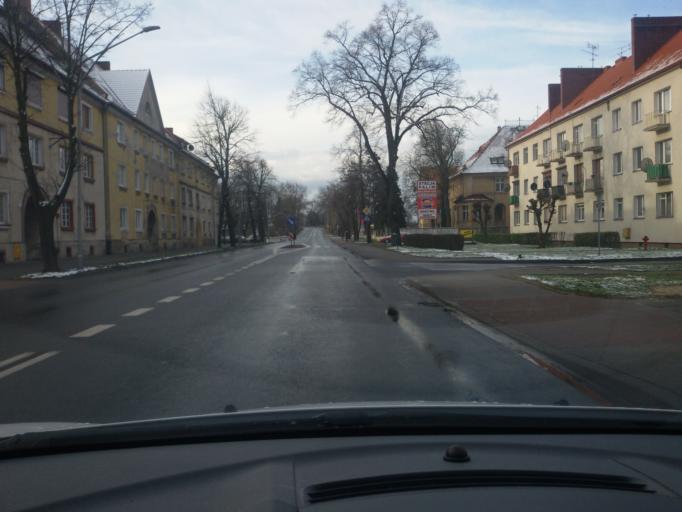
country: PL
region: Lubusz
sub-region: Powiat wschowski
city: Wschowa
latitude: 51.7971
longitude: 16.3146
